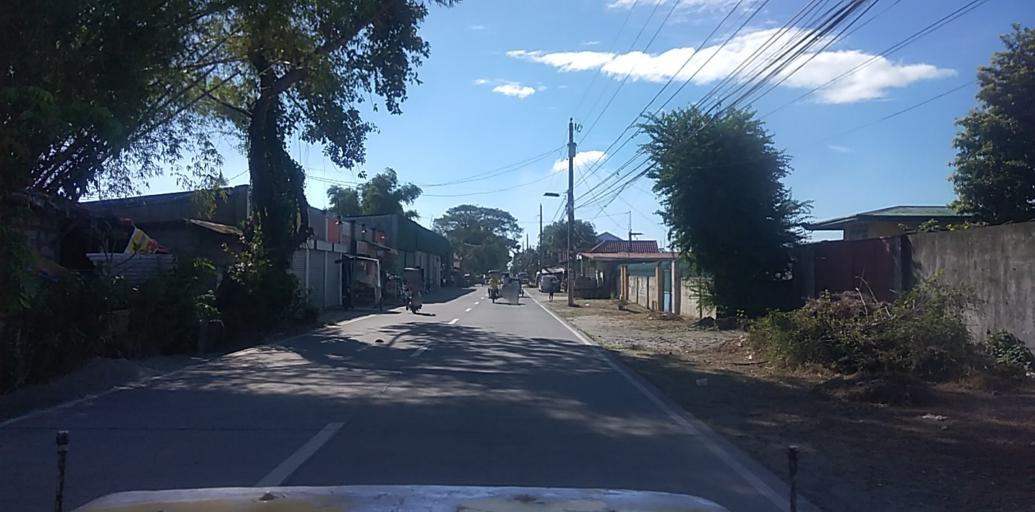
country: PH
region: Central Luzon
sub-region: Province of Pampanga
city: San Patricio
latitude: 15.0908
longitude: 120.7130
